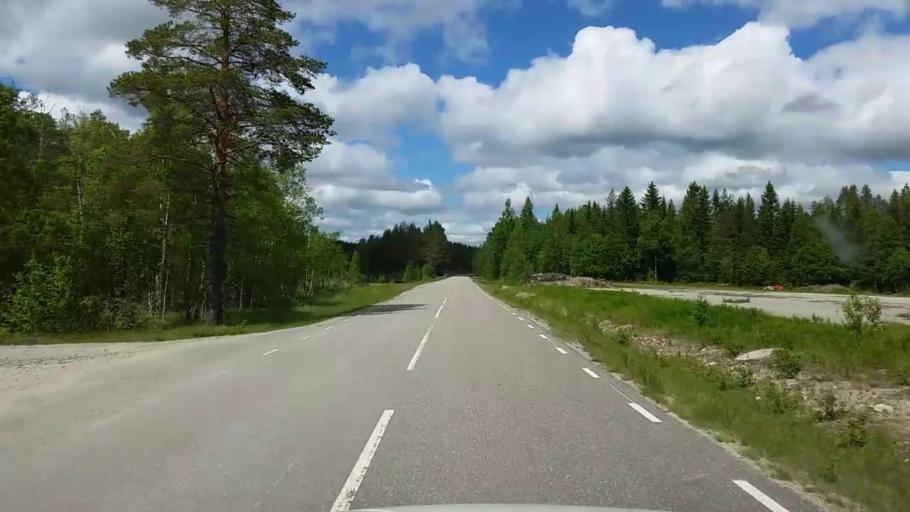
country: SE
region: Gaevleborg
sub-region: Bollnas Kommun
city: Vittsjo
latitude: 61.1490
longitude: 16.1614
